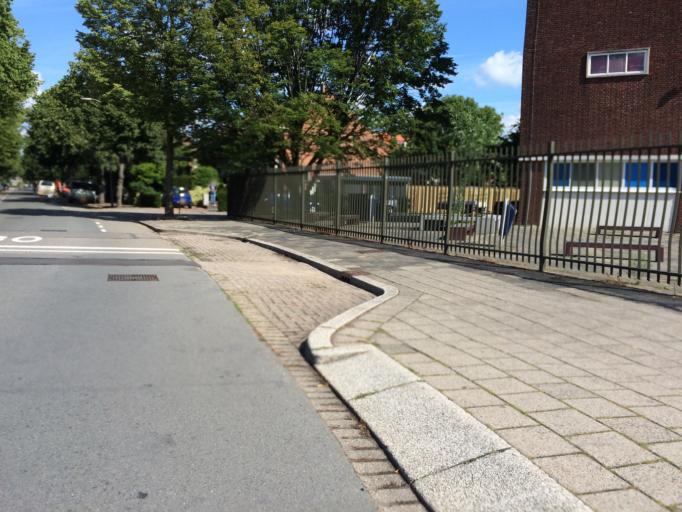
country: NL
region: South Holland
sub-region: Gemeente Dordrecht
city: Dordrecht
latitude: 51.8057
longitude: 4.6888
